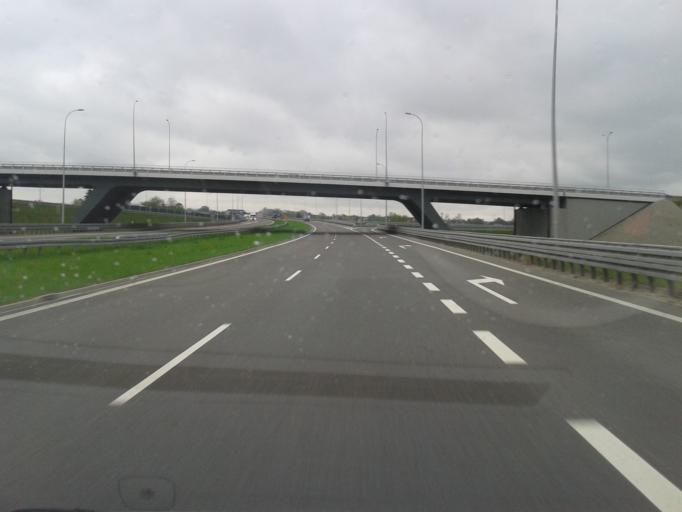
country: PL
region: Subcarpathian Voivodeship
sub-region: Powiat lancucki
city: Lancut
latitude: 50.0996
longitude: 22.2256
